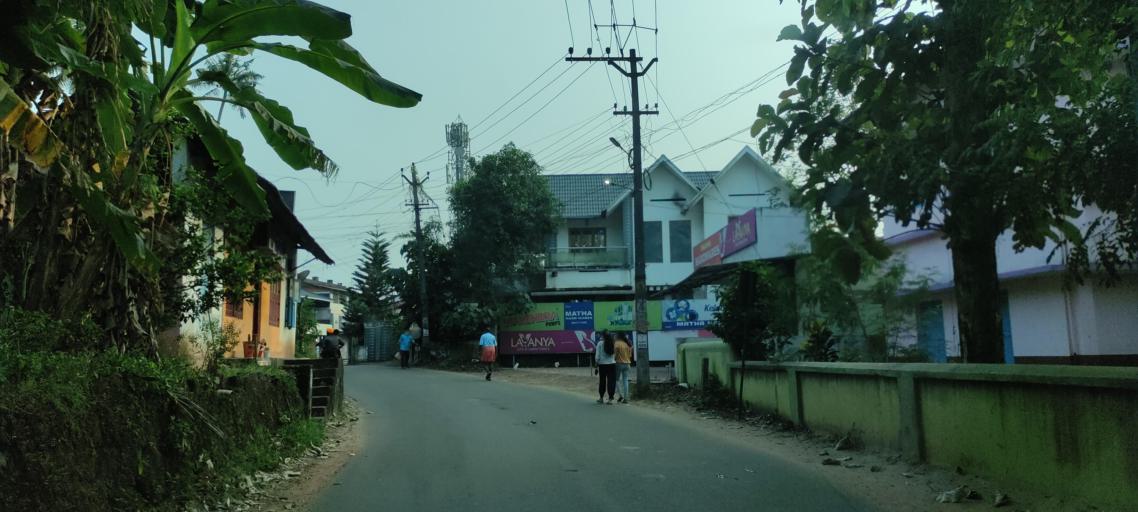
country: IN
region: Kerala
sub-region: Kottayam
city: Vaikam
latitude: 9.6992
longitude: 76.4774
